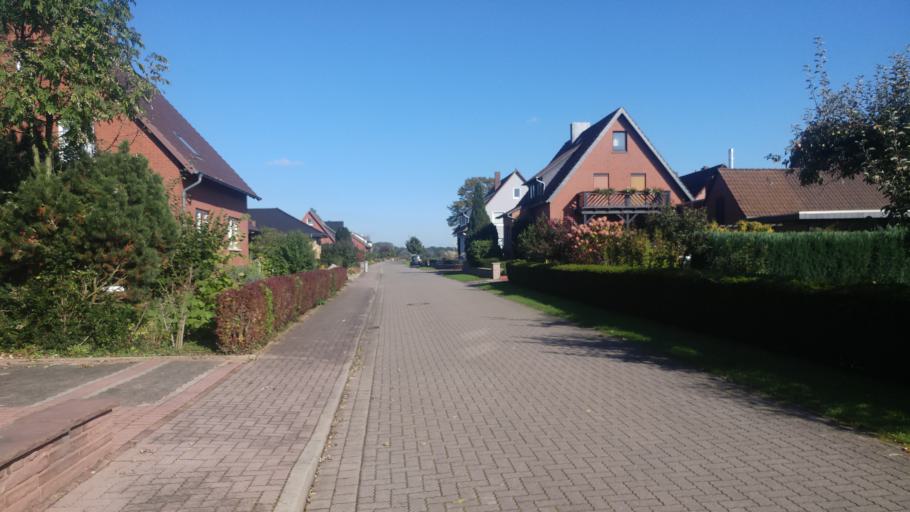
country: DE
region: Lower Saxony
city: Lauenhagen
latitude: 52.3538
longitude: 9.2091
